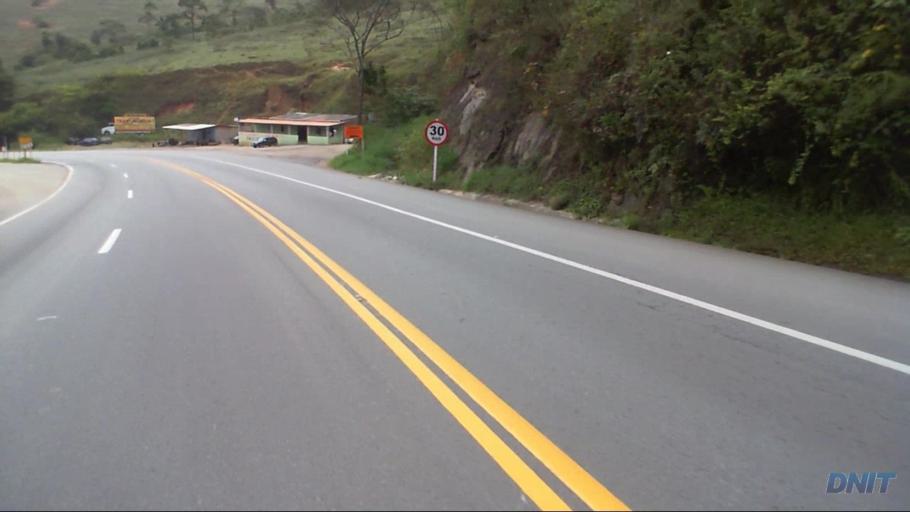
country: BR
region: Minas Gerais
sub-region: Nova Era
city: Nova Era
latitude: -19.6519
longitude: -42.9452
